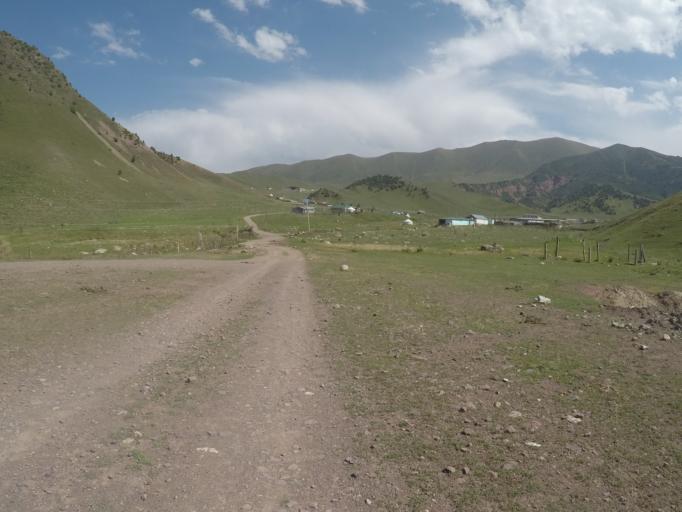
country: KG
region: Chuy
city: Bishkek
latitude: 42.6438
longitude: 74.6151
